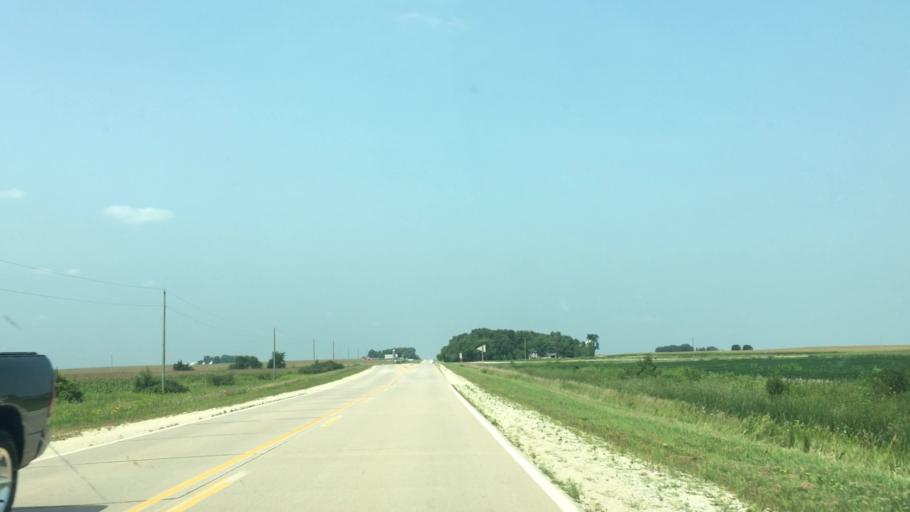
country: US
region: Iowa
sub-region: Fayette County
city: Fayette
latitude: 42.7568
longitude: -91.8043
